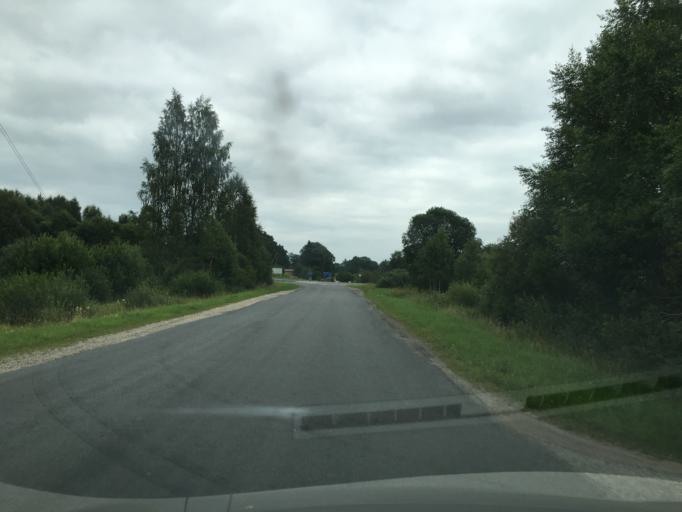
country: EE
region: Raplamaa
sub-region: Kehtna vald
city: Kehtna
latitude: 58.8584
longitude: 24.9964
